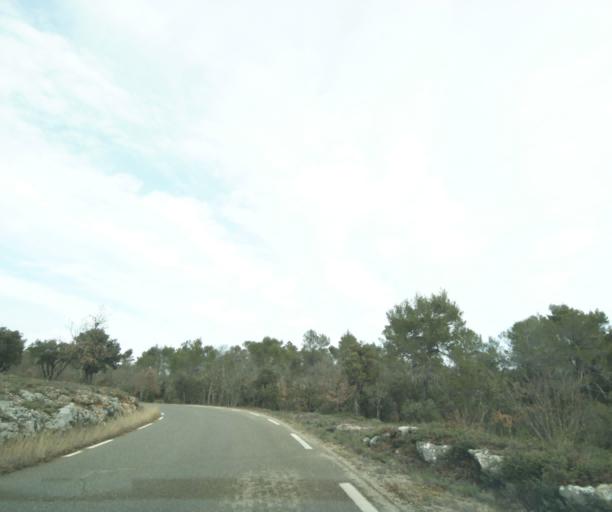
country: FR
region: Provence-Alpes-Cote d'Azur
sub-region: Departement du Var
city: Tourves
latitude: 43.3736
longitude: 5.9002
